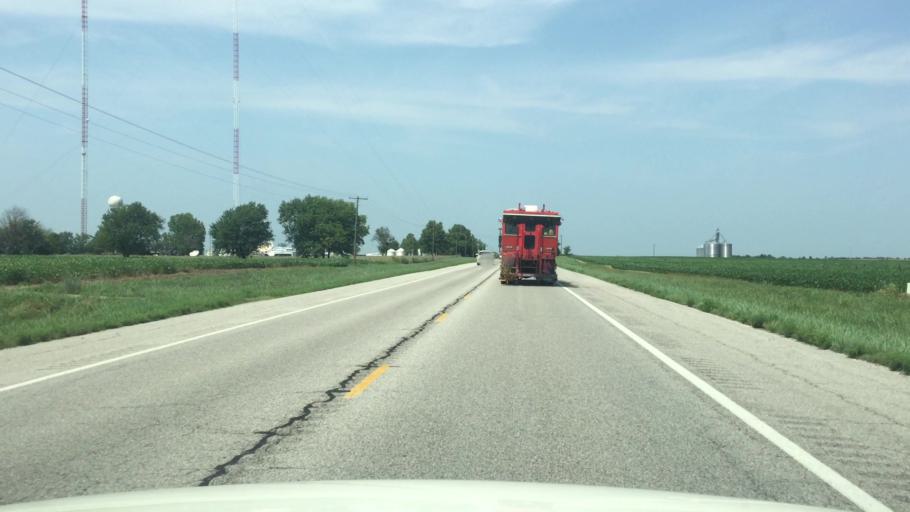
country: US
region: Missouri
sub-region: Jasper County
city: Carl Junction
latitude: 37.2170
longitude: -94.7048
